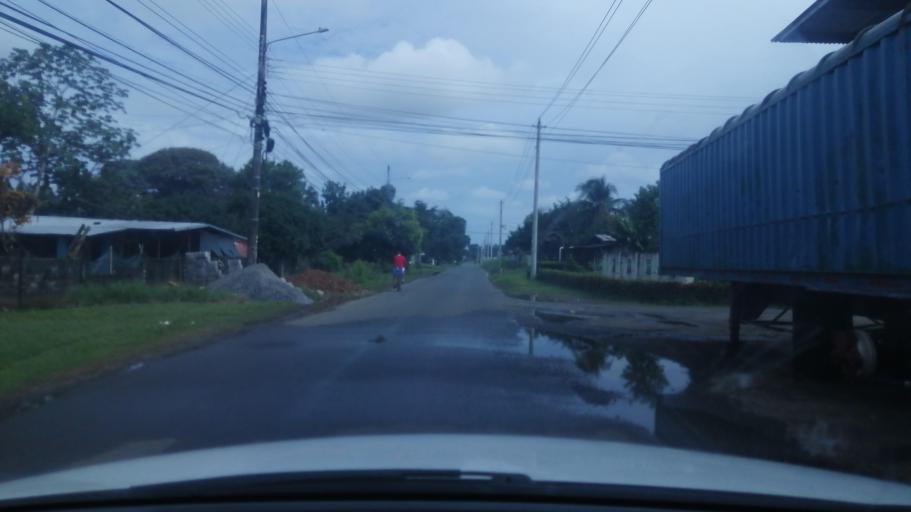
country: PA
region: Chiriqui
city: David
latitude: 8.4088
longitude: -82.4272
